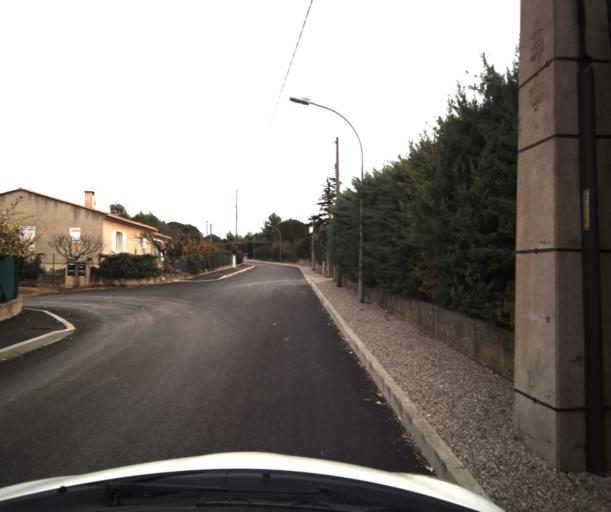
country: FR
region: Provence-Alpes-Cote d'Azur
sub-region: Departement du Vaucluse
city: Pertuis
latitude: 43.6928
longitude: 5.5202
